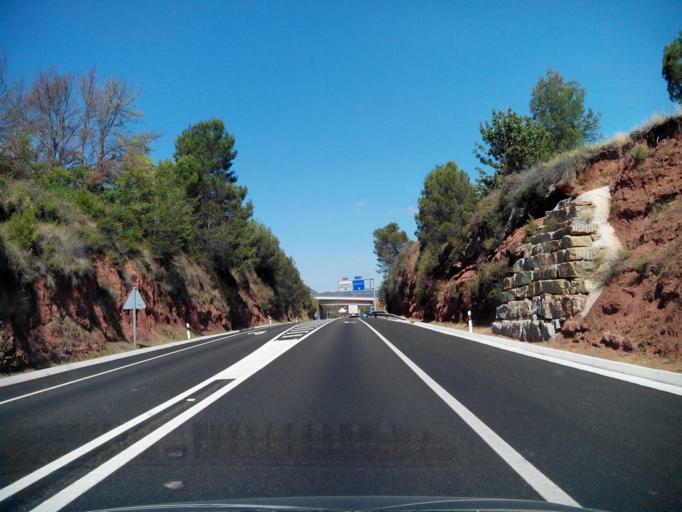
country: ES
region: Catalonia
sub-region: Provincia de Barcelona
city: Olesa de Montserrat
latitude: 41.5890
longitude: 1.9112
